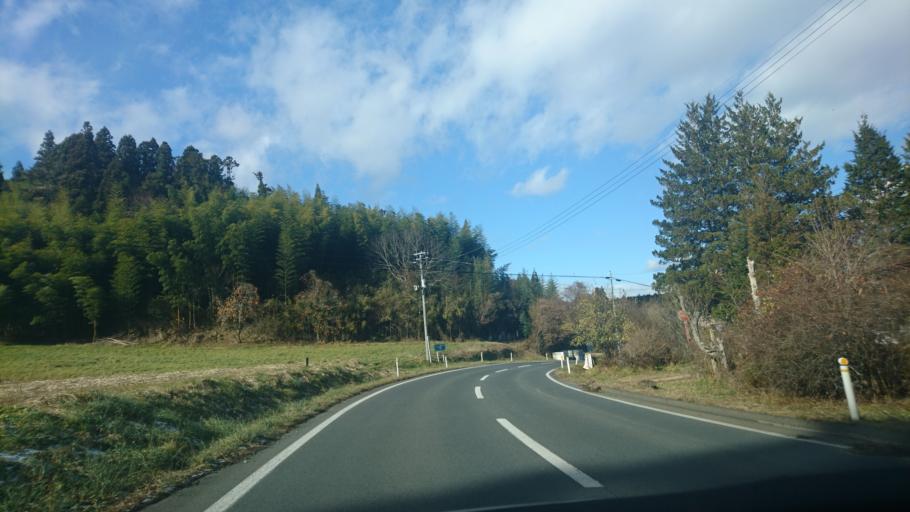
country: JP
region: Iwate
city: Ichinoseki
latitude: 38.9442
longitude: 141.4070
